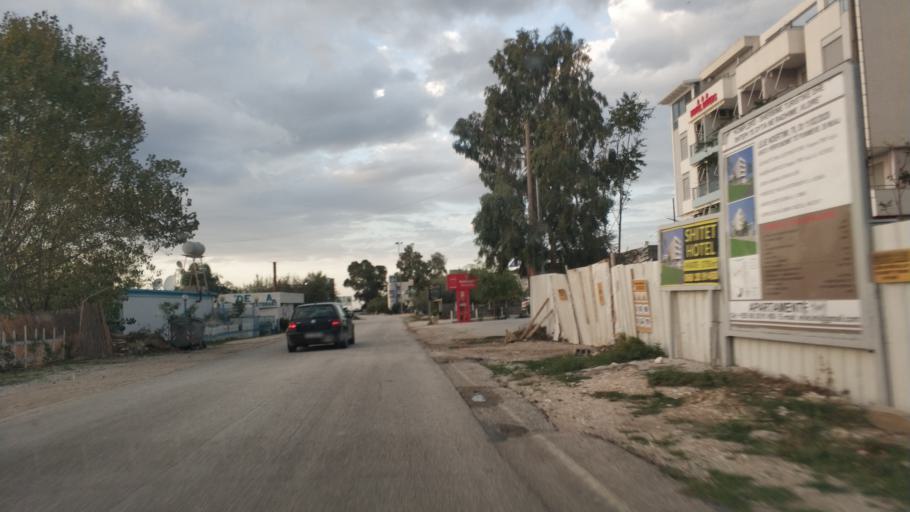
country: AL
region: Vlore
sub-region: Rrethi i Vlores
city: Orikum
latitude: 40.3530
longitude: 19.4850
